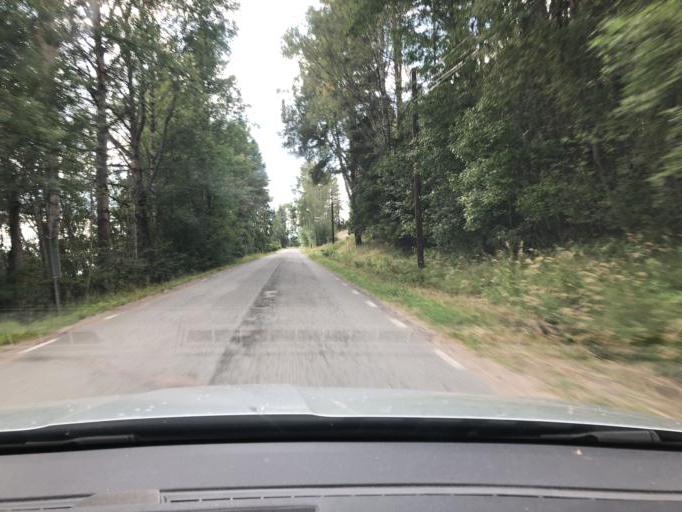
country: SE
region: Vaesternorrland
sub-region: Solleftea Kommun
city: Solleftea
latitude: 63.2116
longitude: 17.1842
